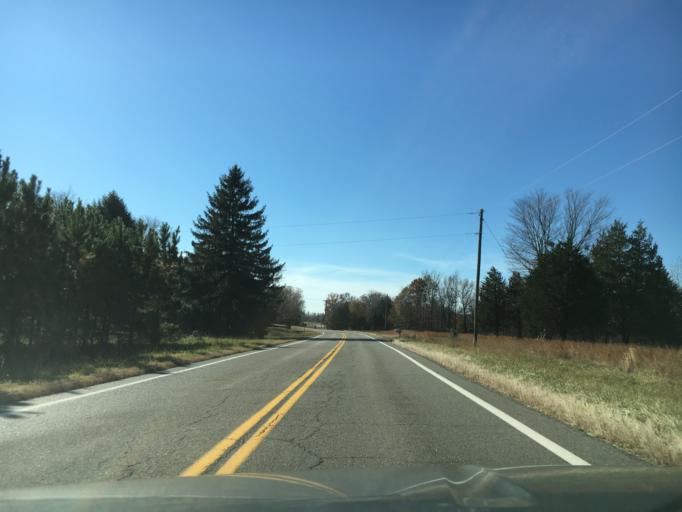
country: US
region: Virginia
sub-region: Cumberland County
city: Cumberland
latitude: 37.6049
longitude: -78.1658
